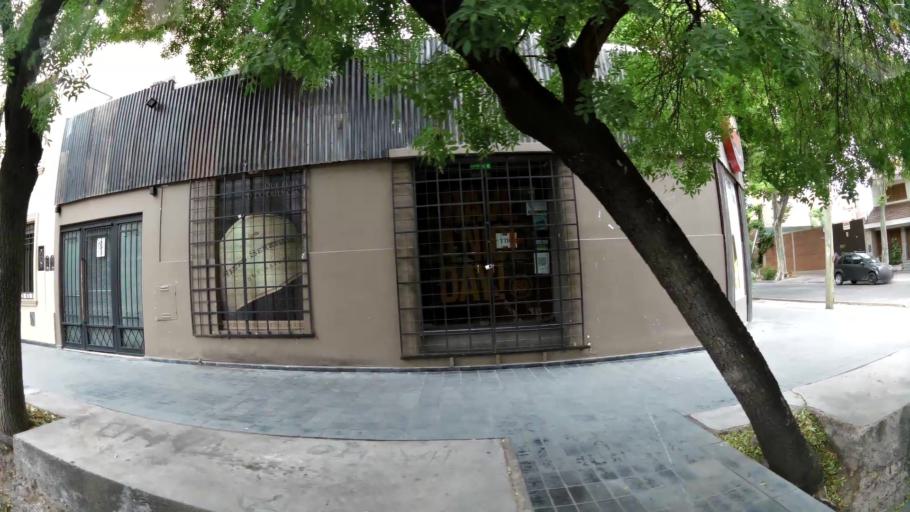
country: AR
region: Mendoza
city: Mendoza
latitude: -32.8870
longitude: -68.8613
